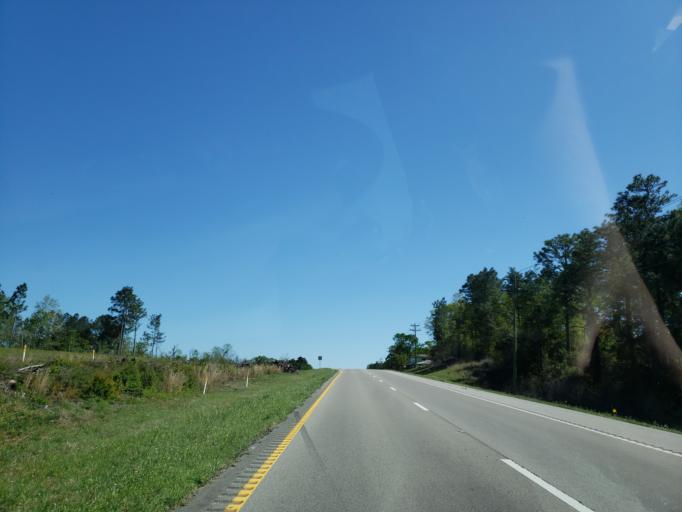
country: US
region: Mississippi
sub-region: Stone County
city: Wiggins
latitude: 30.9228
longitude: -89.1764
